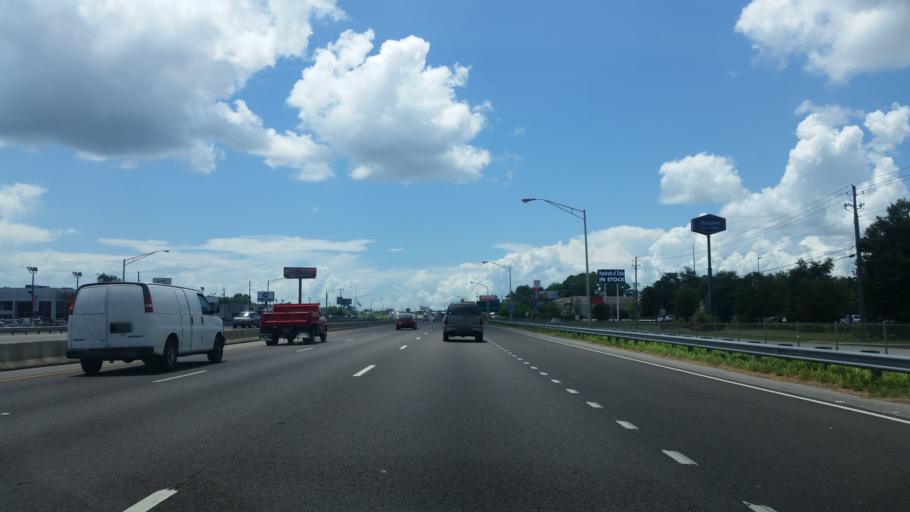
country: US
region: Alabama
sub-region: Mobile County
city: Prichard
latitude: 30.6709
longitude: -88.1274
